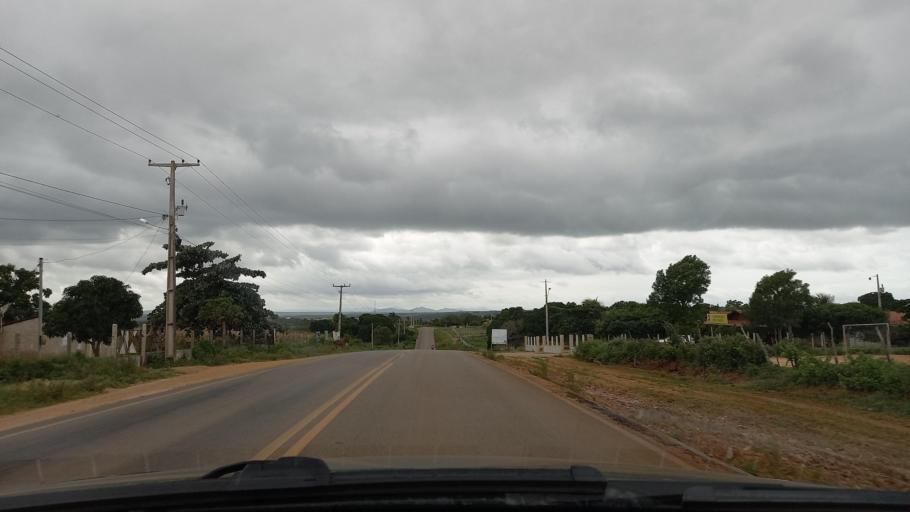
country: BR
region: Sergipe
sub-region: Caninde De Sao Francisco
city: Caninde de Sao Francisco
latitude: -9.6822
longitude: -37.8104
